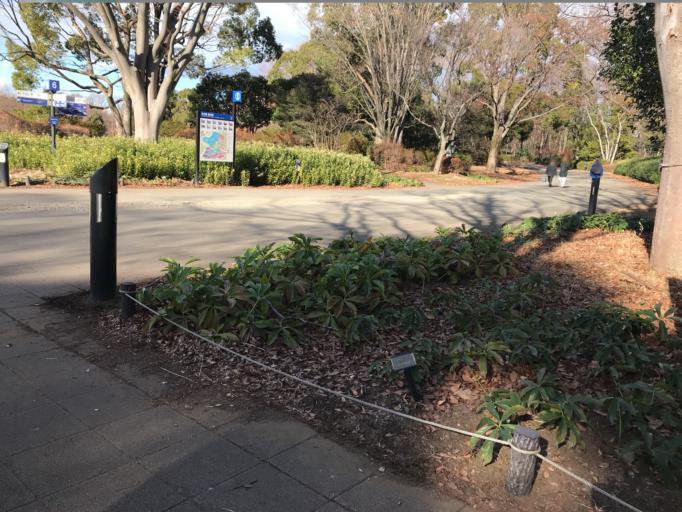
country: JP
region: Tokyo
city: Hino
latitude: 35.7052
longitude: 139.3969
